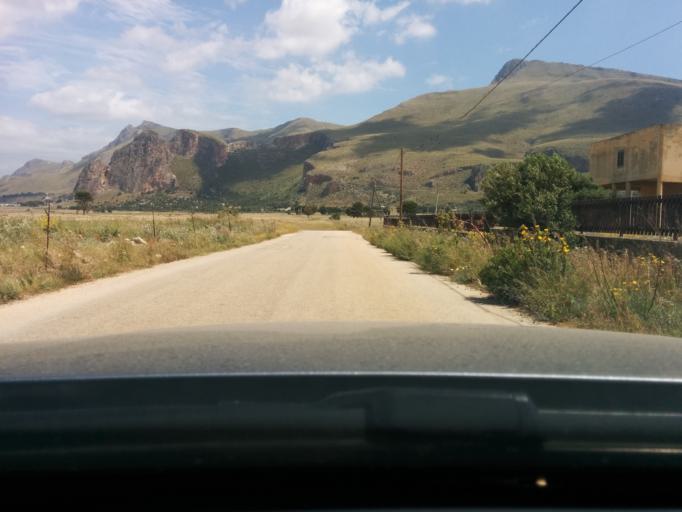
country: IT
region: Sicily
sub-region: Trapani
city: Castelluzzo
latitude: 38.1100
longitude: 12.7236
